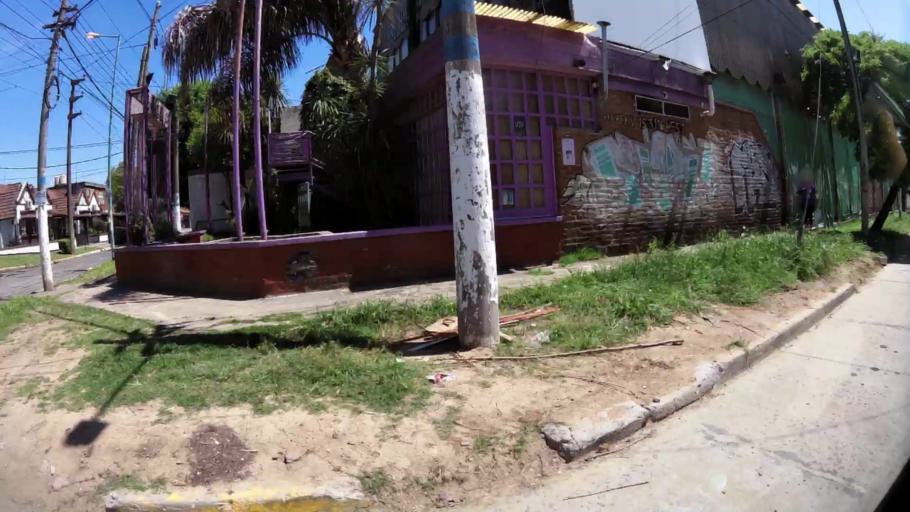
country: AR
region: Buenos Aires
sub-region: Partido de Merlo
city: Merlo
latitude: -34.6672
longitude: -58.6897
